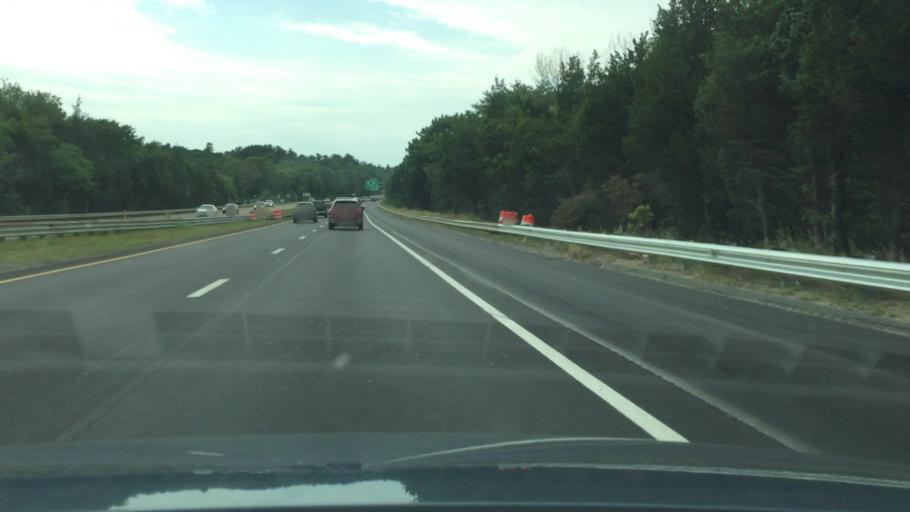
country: US
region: Massachusetts
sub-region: Plymouth County
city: Kingston
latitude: 42.0013
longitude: -70.7229
